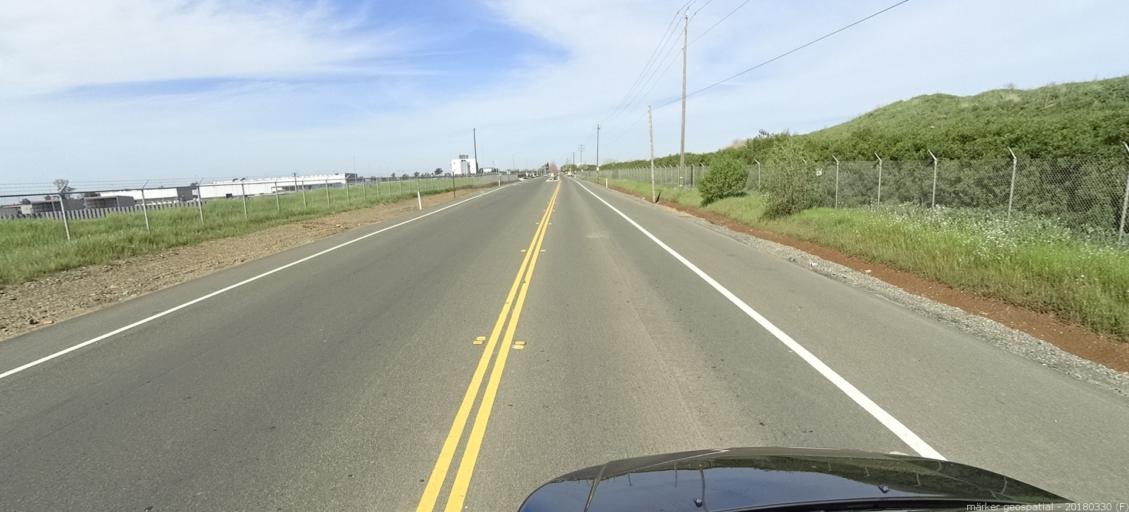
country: US
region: California
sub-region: Sacramento County
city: La Riviera
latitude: 38.5424
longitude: -121.3260
